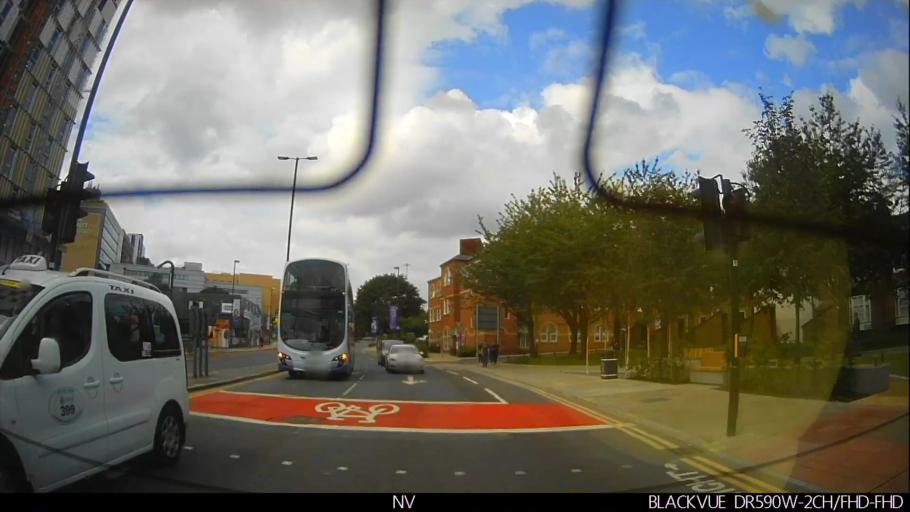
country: GB
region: England
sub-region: City and Borough of Leeds
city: Leeds
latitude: 53.8030
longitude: -1.5461
